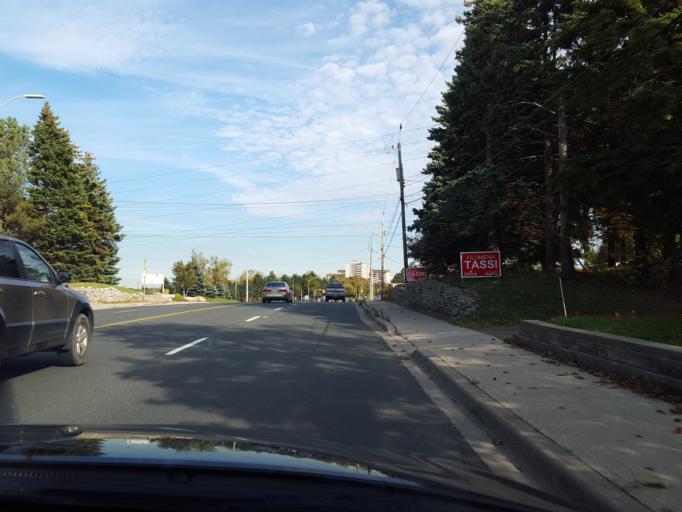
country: CA
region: Ontario
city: Ancaster
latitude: 43.2330
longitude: -79.9328
